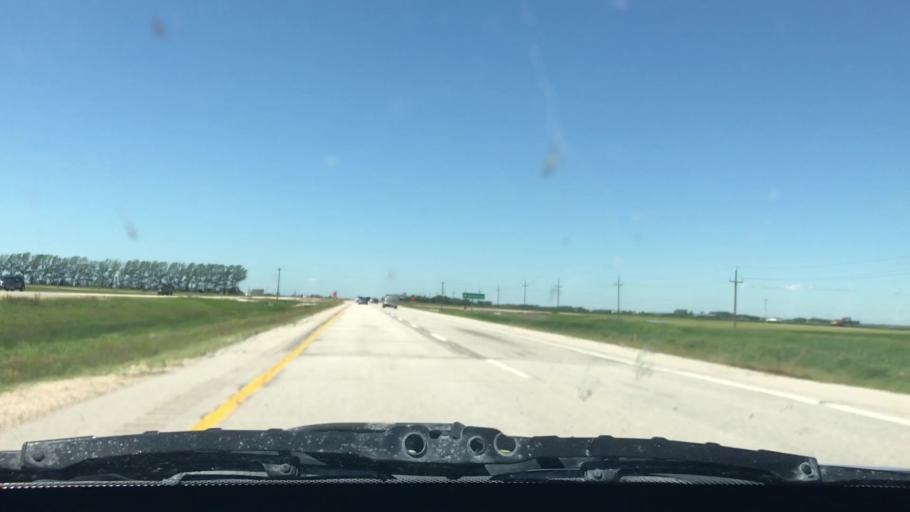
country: CA
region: Manitoba
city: Steinbach
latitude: 49.7322
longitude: -96.7238
